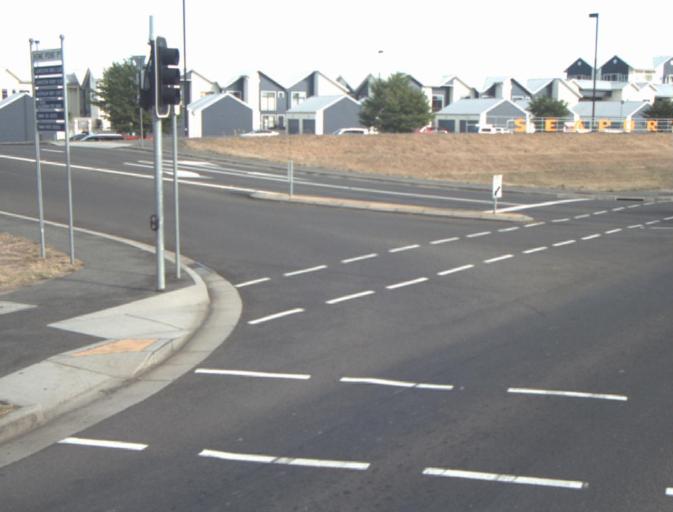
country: AU
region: Tasmania
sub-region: Launceston
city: Launceston
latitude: -41.4350
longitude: 147.1333
